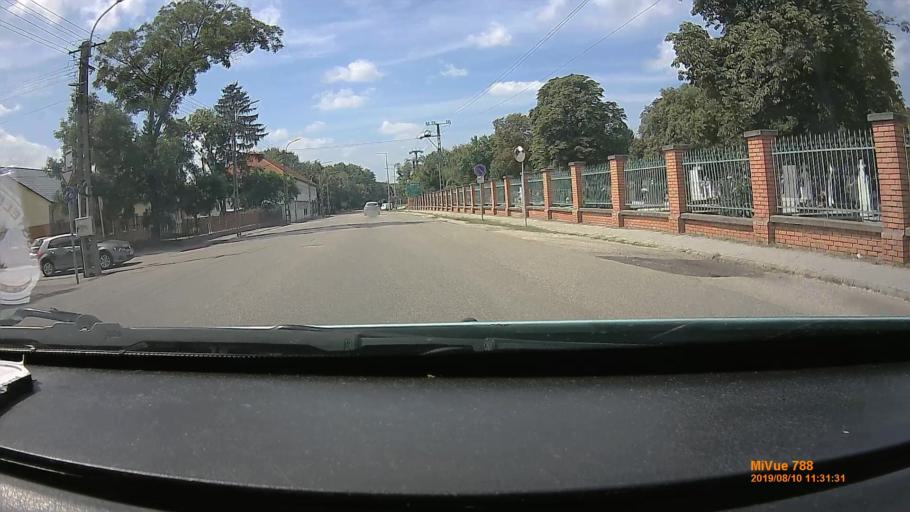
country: HU
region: Borsod-Abauj-Zemplen
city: Mezokovesd
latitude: 47.8146
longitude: 20.5829
